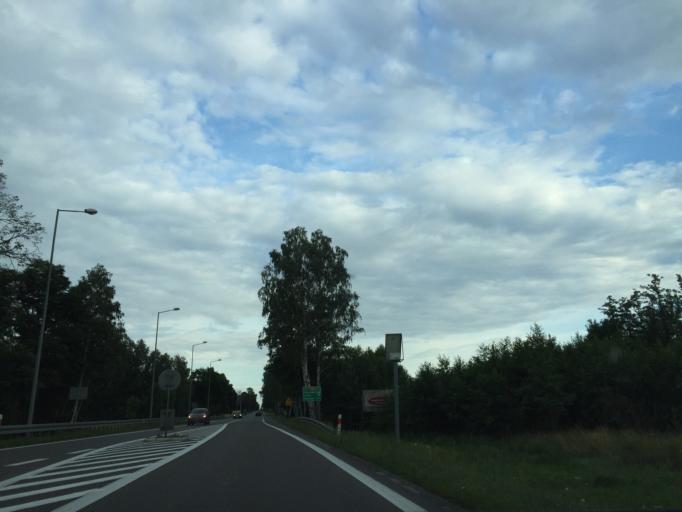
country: PL
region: Lublin Voivodeship
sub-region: Powiat lubartowski
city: Kock
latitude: 51.5981
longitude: 22.4743
